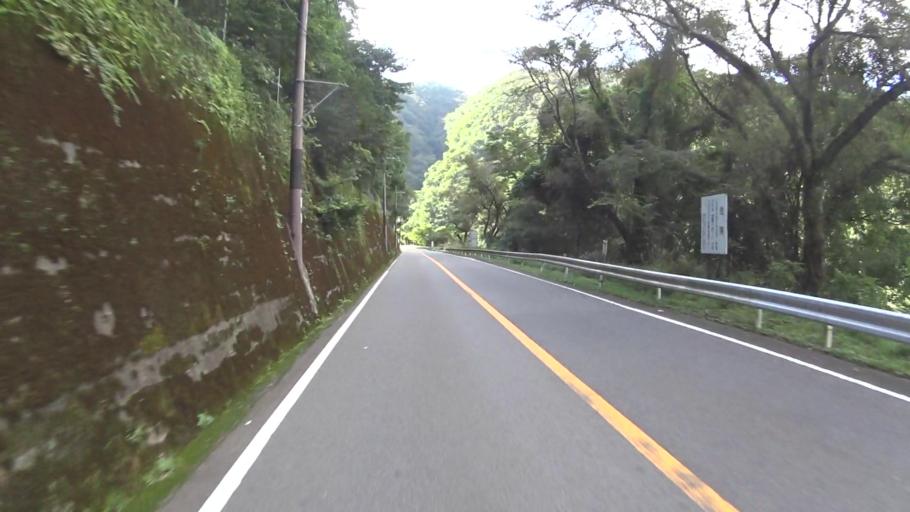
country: JP
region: Kyoto
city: Uji
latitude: 34.8826
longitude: 135.8570
